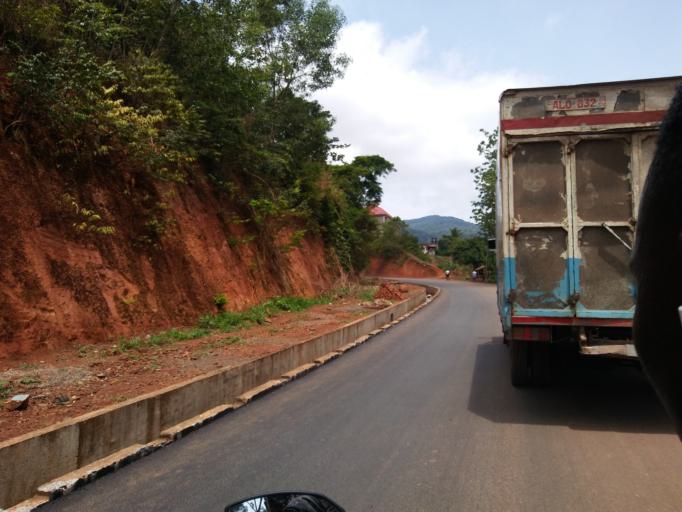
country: SL
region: Western Area
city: Hastings
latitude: 8.3990
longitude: -13.1532
